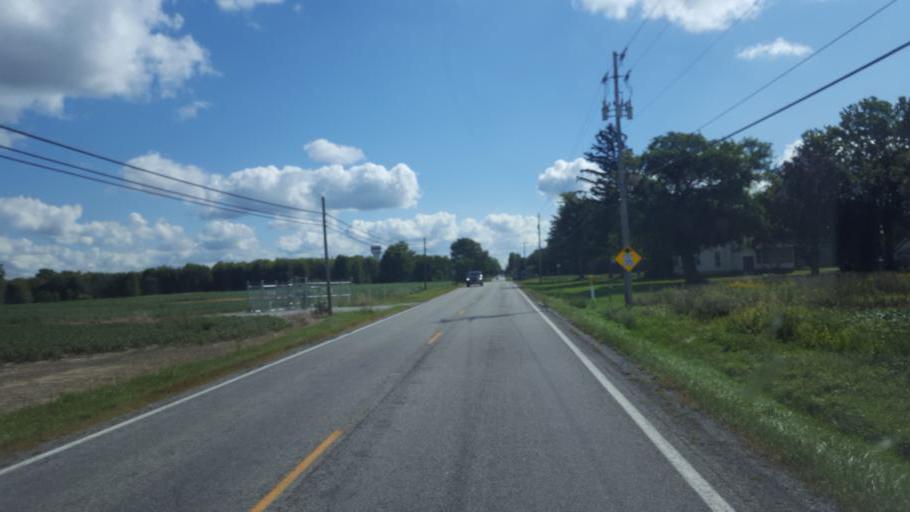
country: US
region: Ohio
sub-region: Lorain County
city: Lagrange
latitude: 41.2372
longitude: -82.1319
